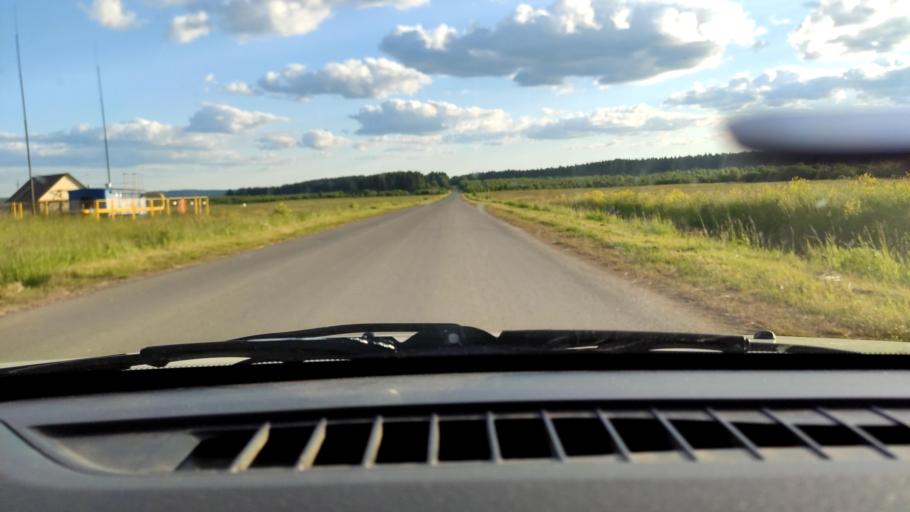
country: RU
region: Perm
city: Uinskoye
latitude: 57.0932
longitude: 56.6378
